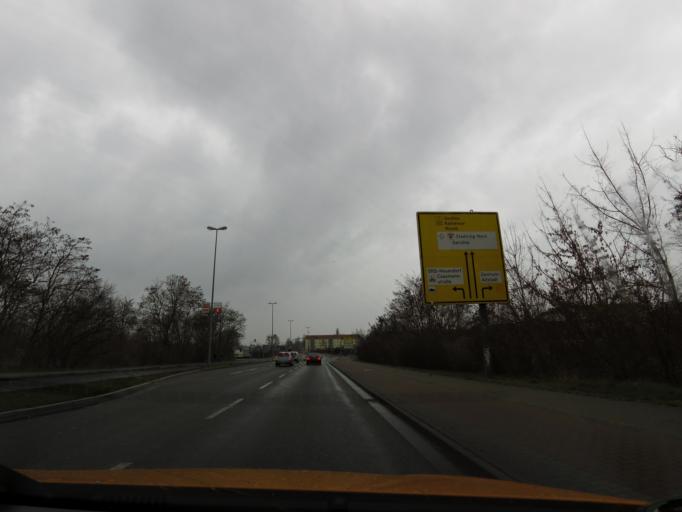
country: DE
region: Brandenburg
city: Brandenburg an der Havel
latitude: 52.4053
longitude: 12.5379
